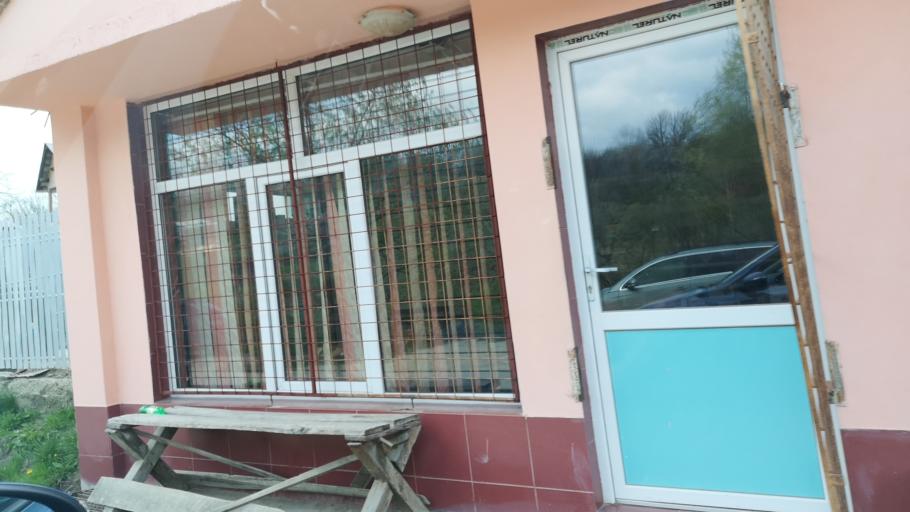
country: RO
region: Prahova
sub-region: Comuna Soimari
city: Soimari
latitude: 45.1801
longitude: 26.2174
